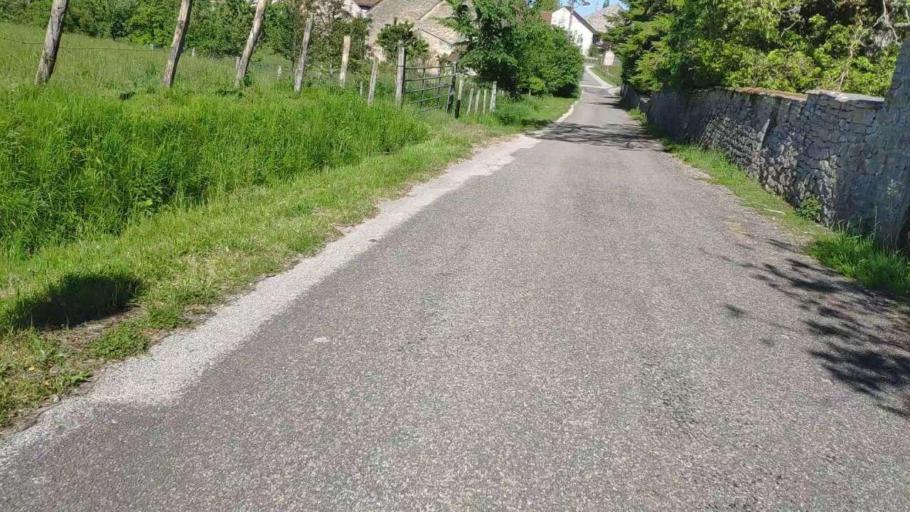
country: FR
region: Franche-Comte
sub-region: Departement du Jura
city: Clairvaux-les-Lacs
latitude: 46.6993
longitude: 5.7312
